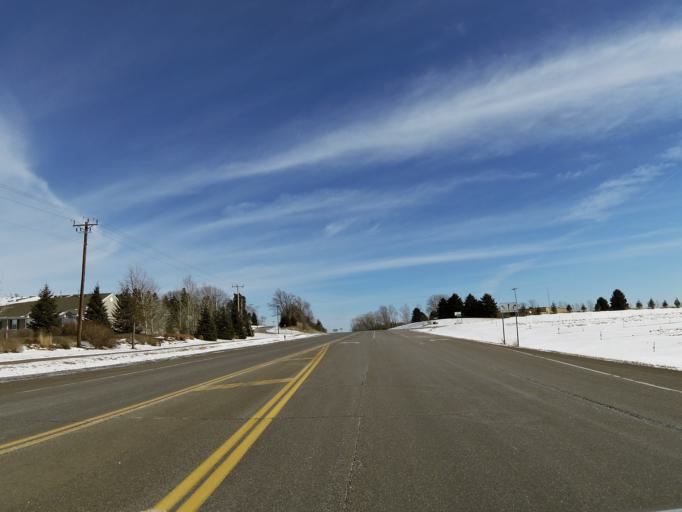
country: US
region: Minnesota
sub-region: Washington County
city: Woodbury
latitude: 44.8909
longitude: -92.8850
